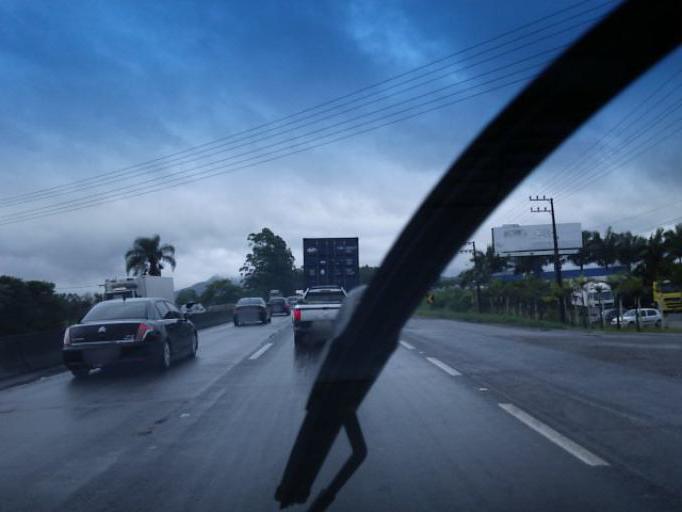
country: BR
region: Santa Catarina
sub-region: Itajai
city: Itajai
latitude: -26.9337
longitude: -48.7015
